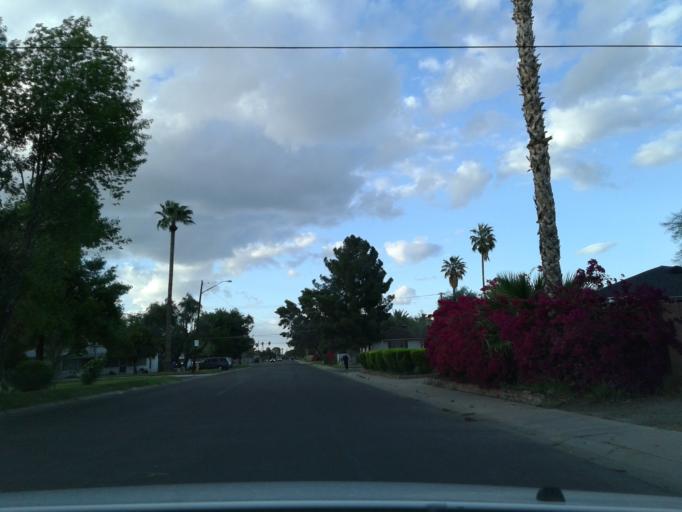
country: US
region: Arizona
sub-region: Maricopa County
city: Phoenix
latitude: 33.5026
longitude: -112.1041
